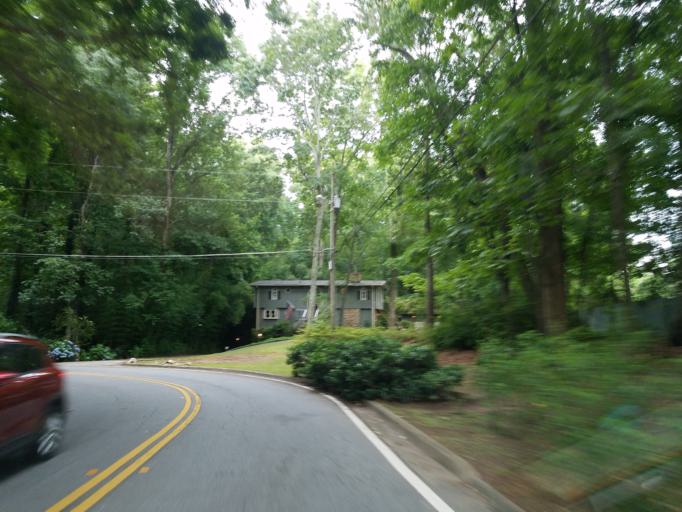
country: US
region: Georgia
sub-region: Cobb County
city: Fair Oaks
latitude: 33.9310
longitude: -84.5705
